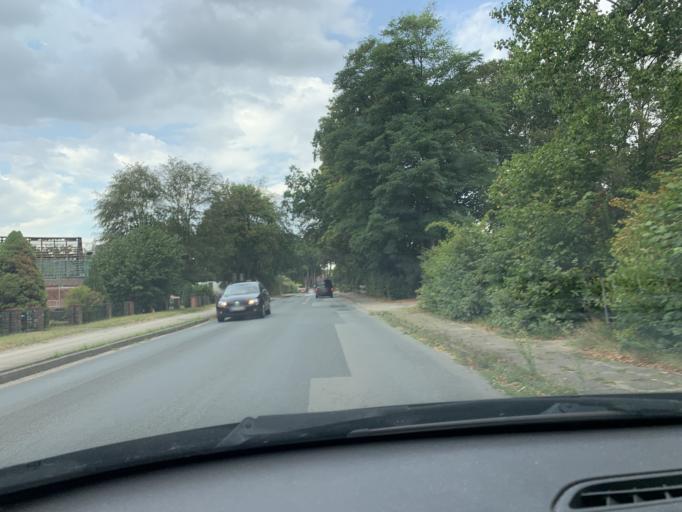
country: DE
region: Lower Saxony
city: Heidenau
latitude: 53.3131
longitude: 9.6607
